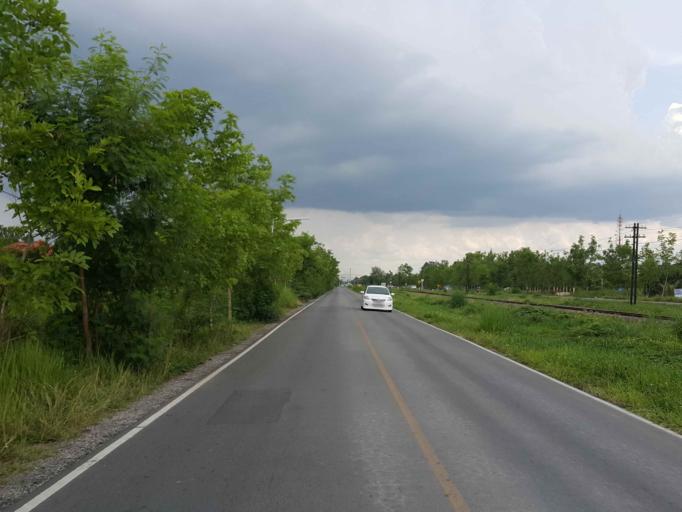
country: TH
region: Chiang Mai
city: Saraphi
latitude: 18.7203
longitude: 99.0376
